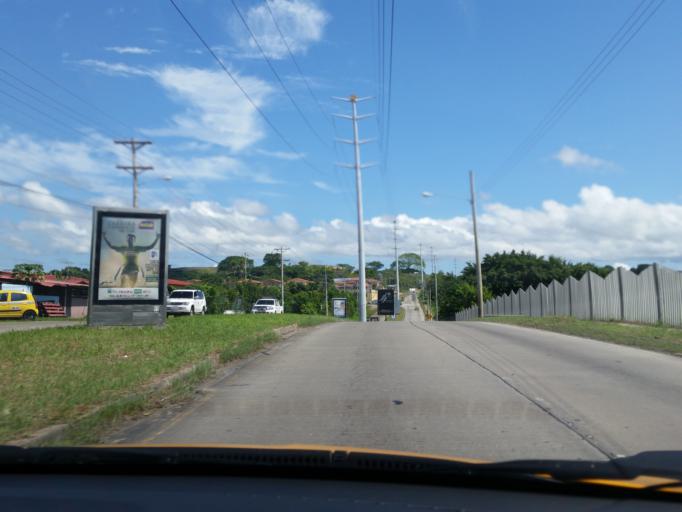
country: PA
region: Panama
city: San Miguelito
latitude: 9.0555
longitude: -79.4615
